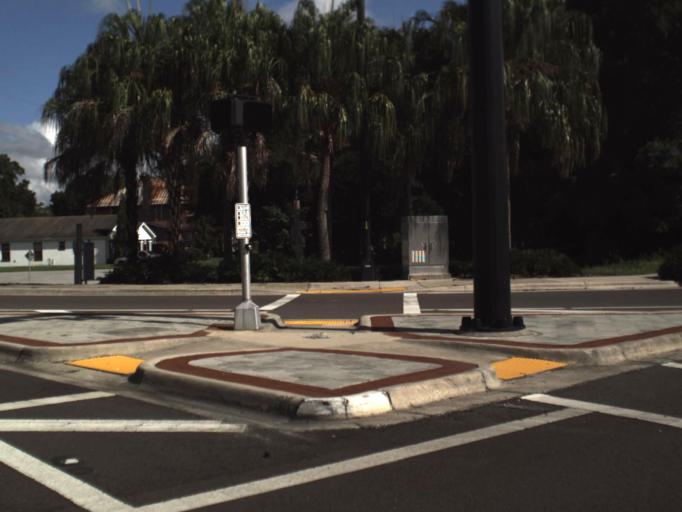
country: US
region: Florida
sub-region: Polk County
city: Lakeland
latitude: 28.0484
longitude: -81.9639
